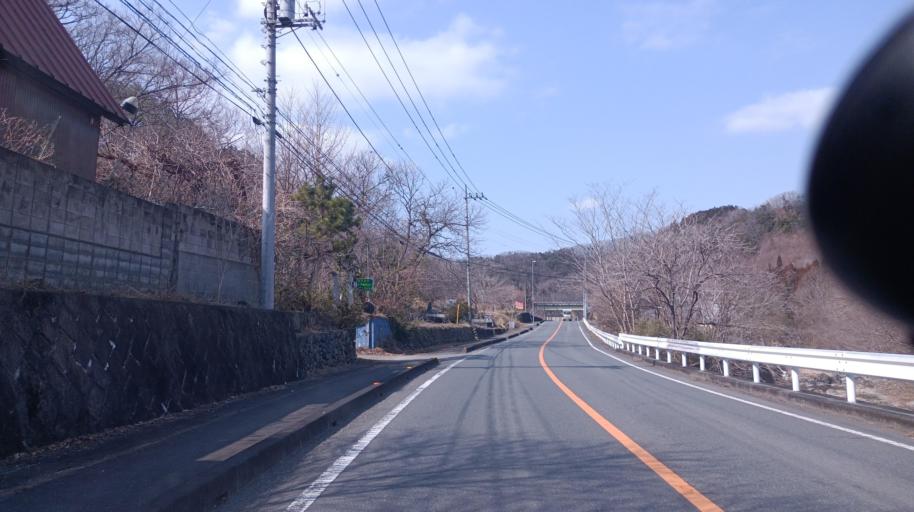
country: JP
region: Saitama
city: Yorii
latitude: 36.0719
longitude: 139.1202
